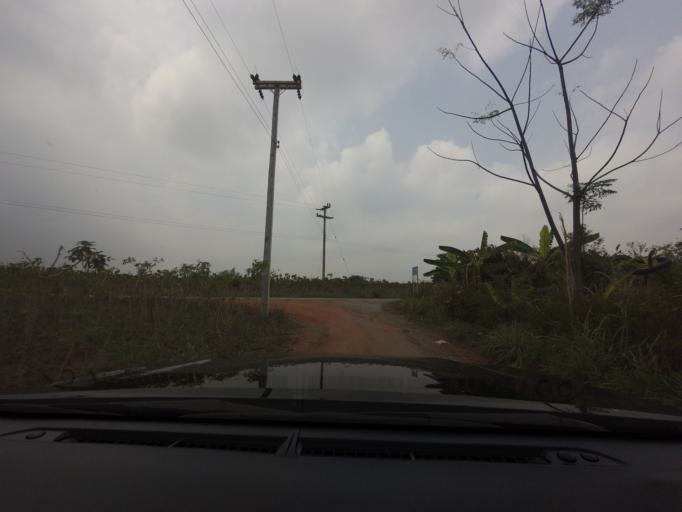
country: TH
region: Nakhon Ratchasima
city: Wang Nam Khiao
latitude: 14.4770
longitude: 101.6442
